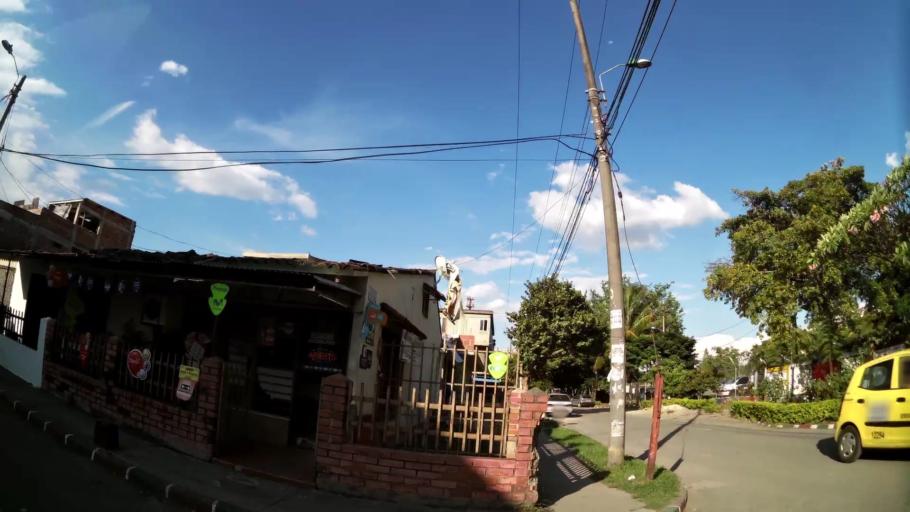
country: CO
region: Valle del Cauca
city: Cali
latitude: 3.4050
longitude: -76.5049
